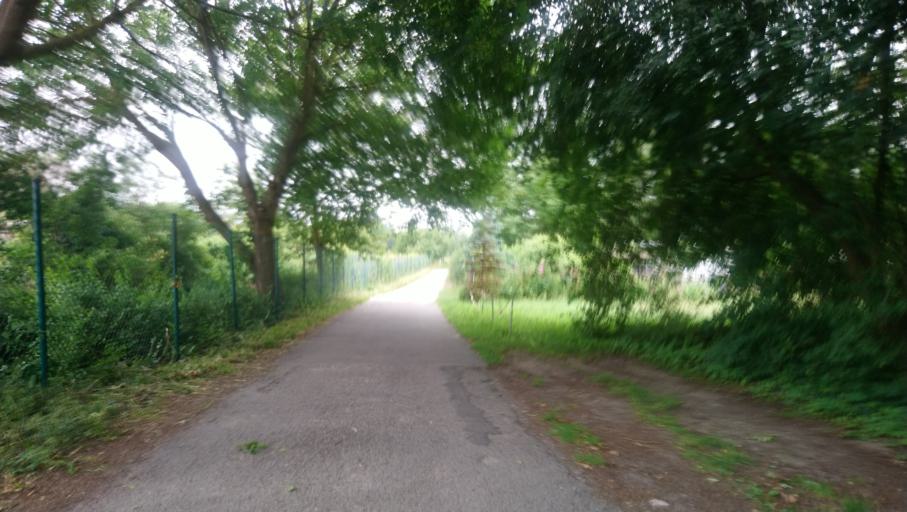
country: DE
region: Mecklenburg-Vorpommern
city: Rostock
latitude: 54.0717
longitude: 12.0996
